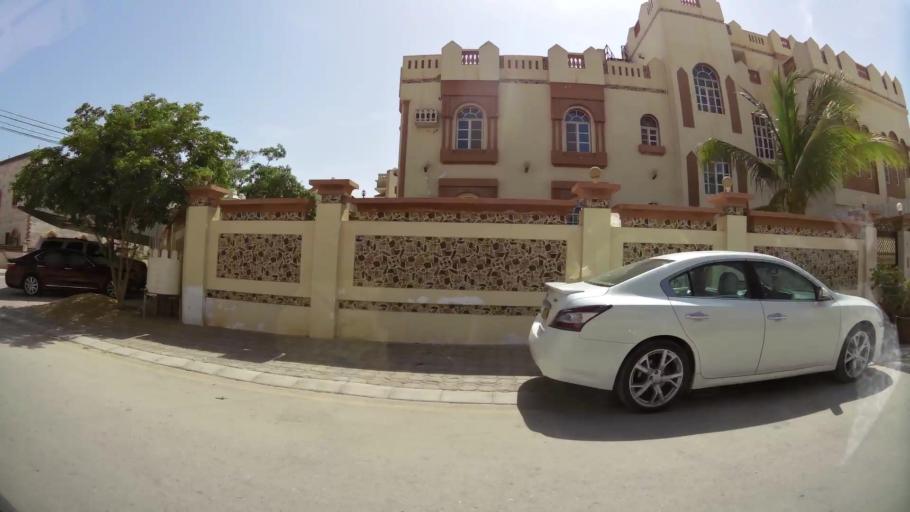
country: OM
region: Zufar
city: Salalah
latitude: 17.0448
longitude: 54.1602
